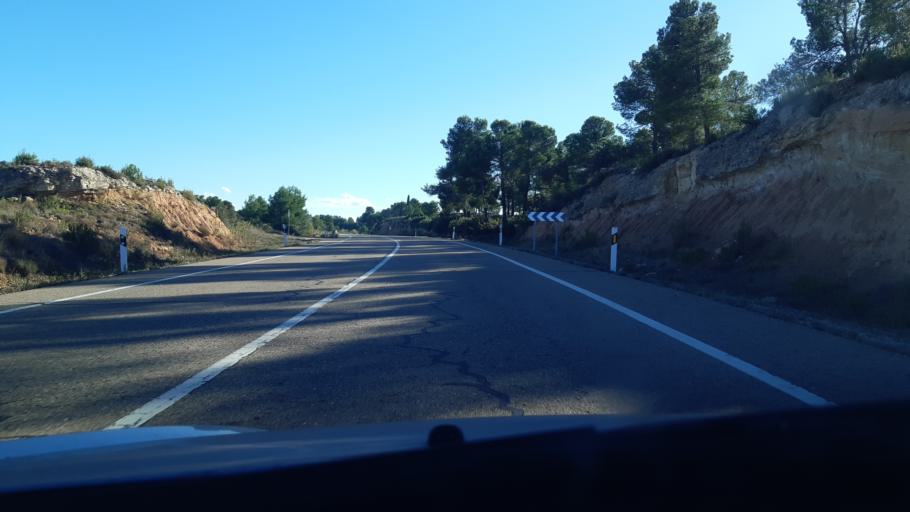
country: ES
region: Aragon
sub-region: Provincia de Teruel
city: Valjunquera
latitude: 40.9420
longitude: -0.0121
